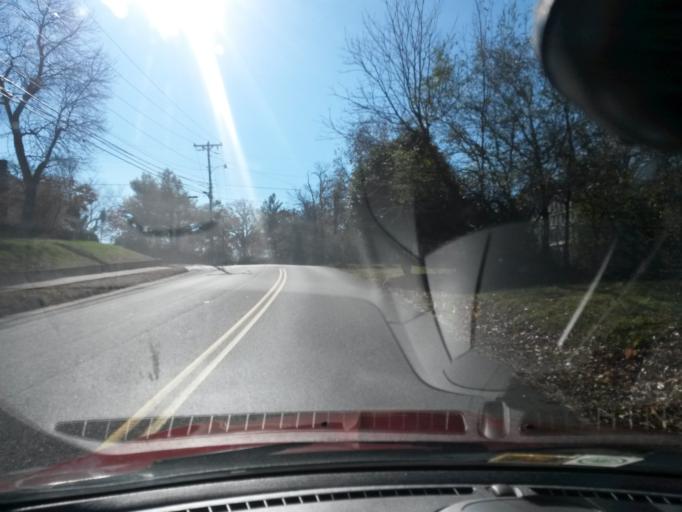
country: US
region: Virginia
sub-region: City of Bedford
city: Bedford
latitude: 37.3459
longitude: -79.5277
